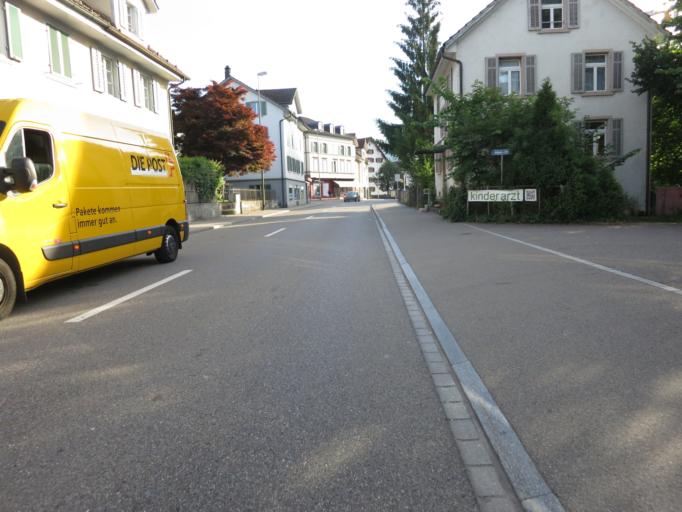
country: CH
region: Zurich
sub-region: Bezirk Hinwil
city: Rueti / Westlicher Dorfteil
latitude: 47.2581
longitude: 8.8476
